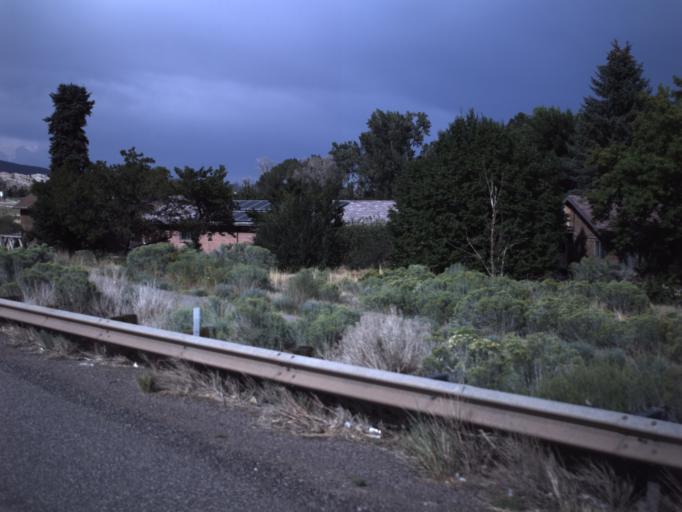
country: US
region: Utah
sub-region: Sevier County
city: Monroe
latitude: 38.5818
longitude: -112.2582
